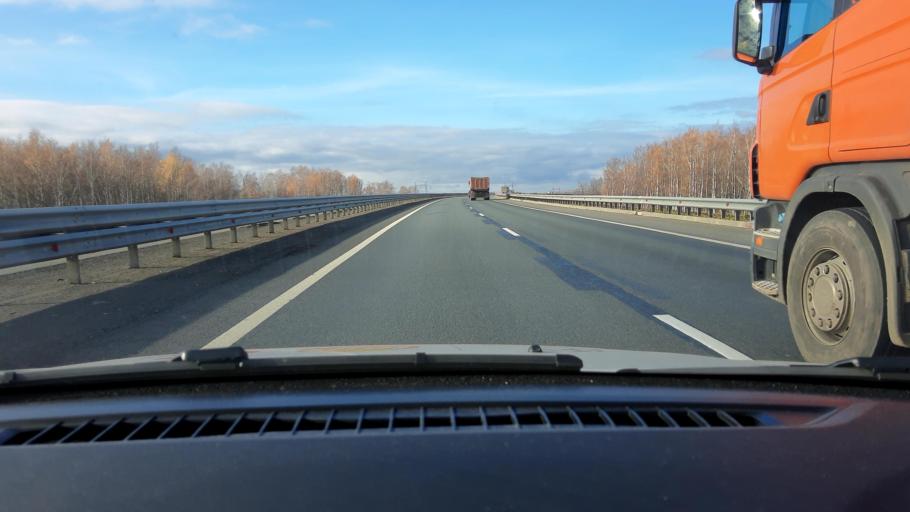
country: RU
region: Nizjnij Novgorod
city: Burevestnik
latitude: 56.1140
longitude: 43.8447
